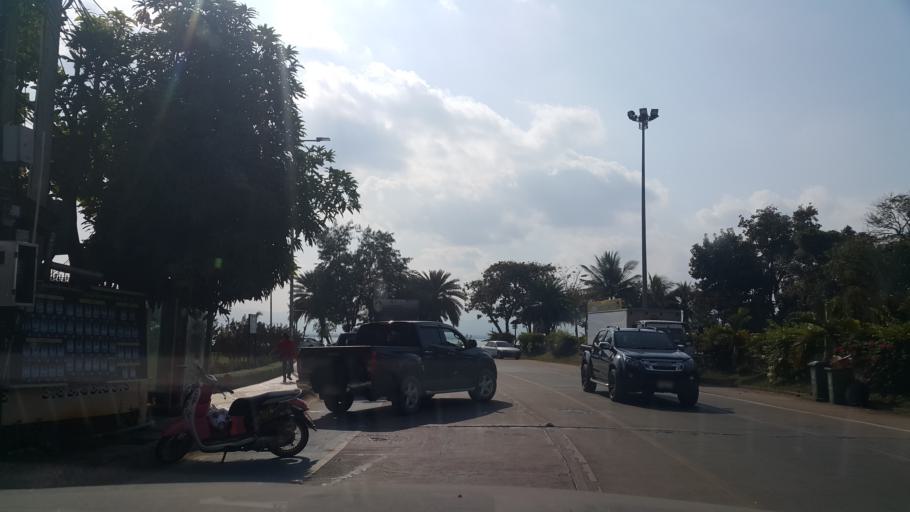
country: TH
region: Phayao
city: Phayao
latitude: 19.1697
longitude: 99.8957
